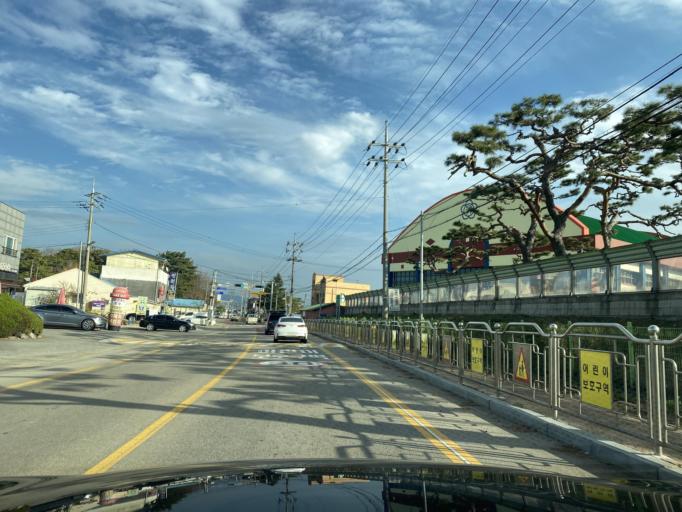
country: KR
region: Chungcheongnam-do
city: Yesan
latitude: 36.6883
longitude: 126.7938
